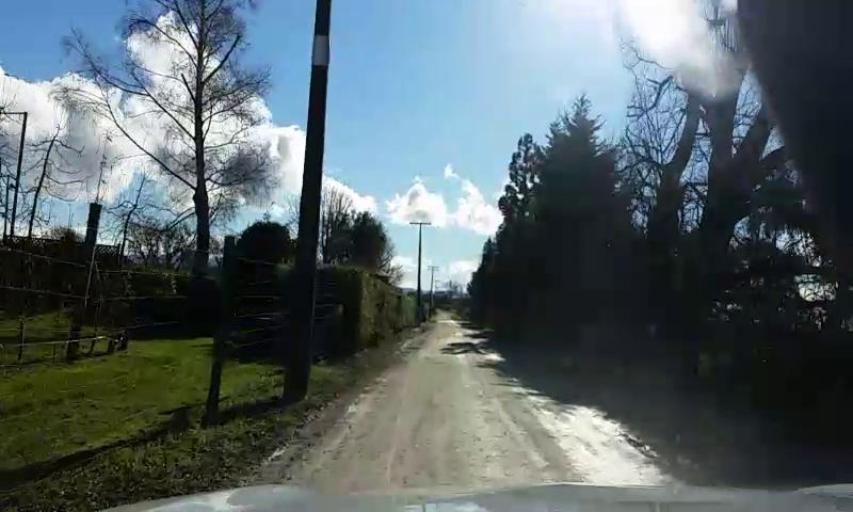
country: NZ
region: Tasman
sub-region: Tasman District
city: Richmond
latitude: -41.3014
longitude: 173.1428
